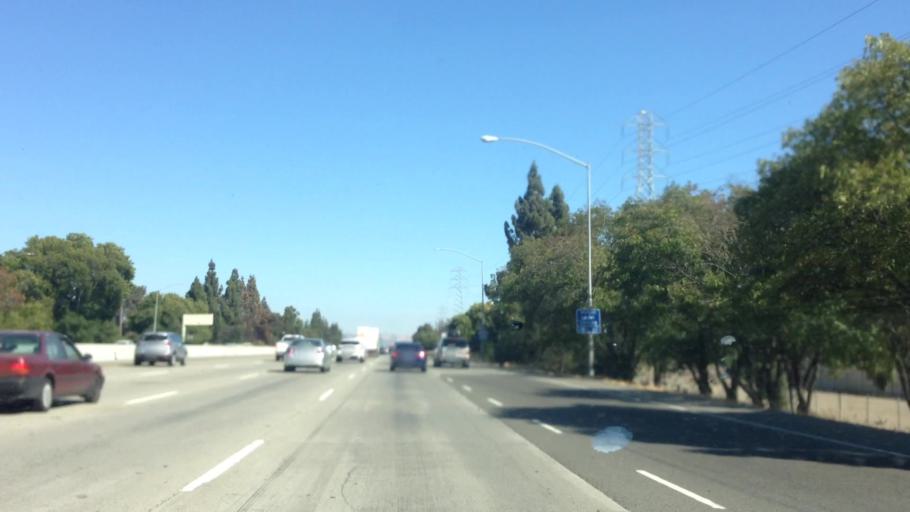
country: US
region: California
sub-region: Santa Clara County
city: Alum Rock
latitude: 37.3814
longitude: -121.8599
